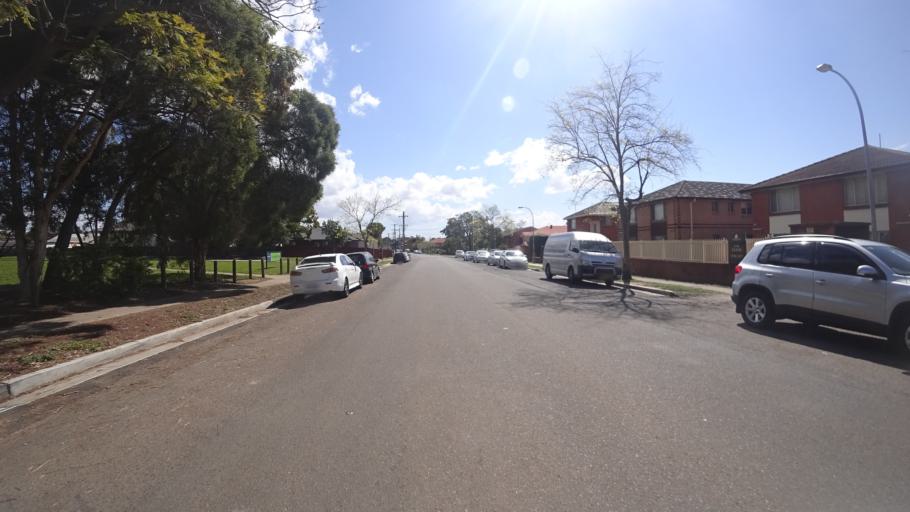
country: AU
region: New South Wales
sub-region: Fairfield
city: Chipping Norton
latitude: -33.8932
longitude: 150.9437
